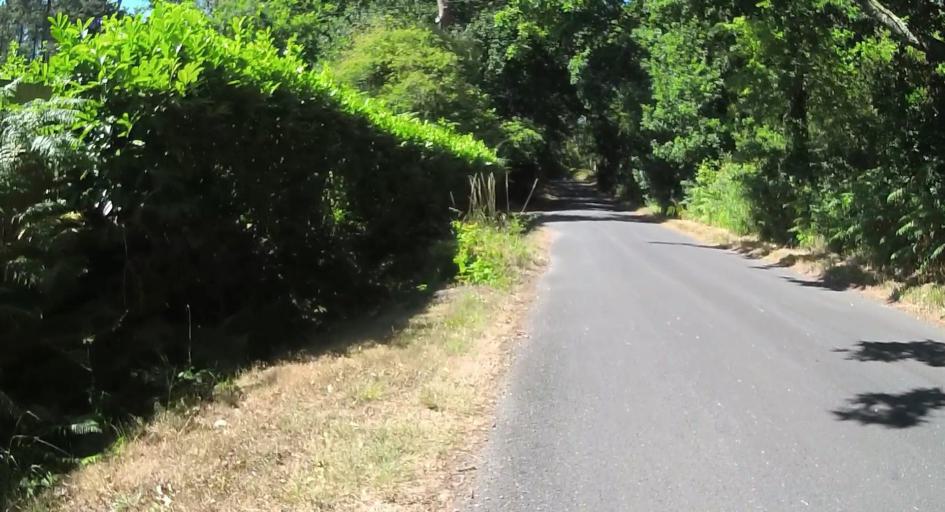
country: GB
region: England
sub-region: Dorset
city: Bovington Camp
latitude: 50.7317
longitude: -2.2603
